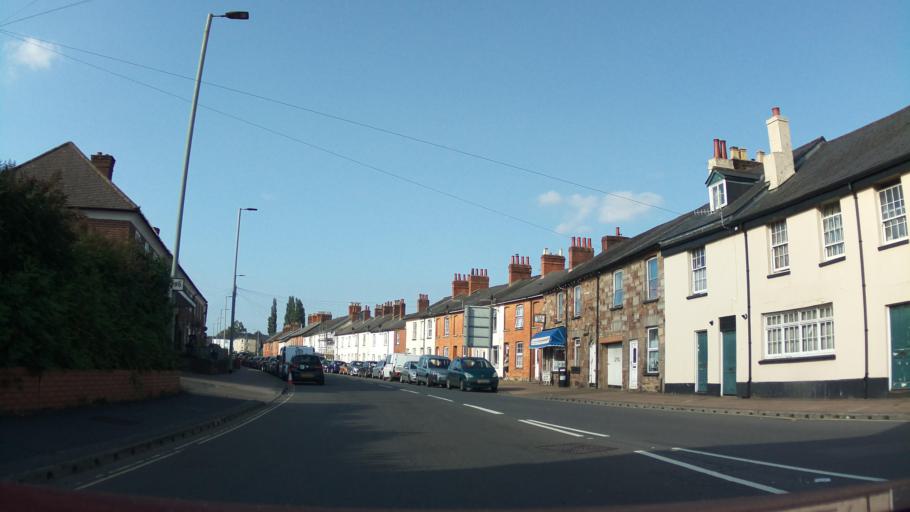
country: GB
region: England
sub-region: Devon
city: Tiverton
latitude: 50.9000
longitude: -3.4911
